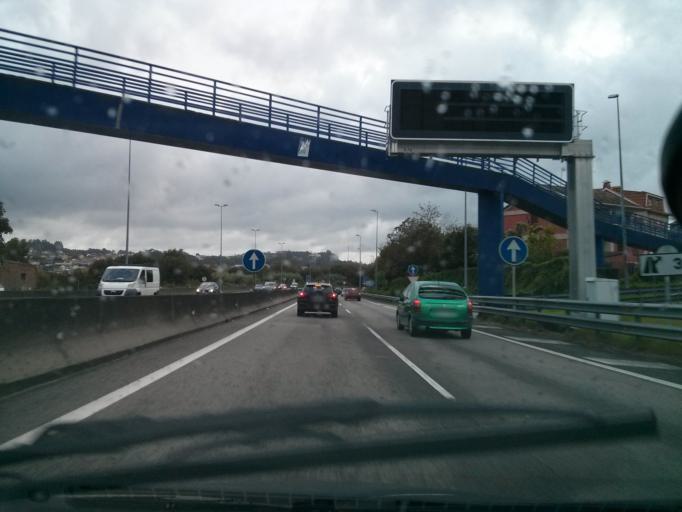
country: ES
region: Galicia
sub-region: Provincia de Pontevedra
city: Vigo
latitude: 42.2070
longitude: -8.6928
